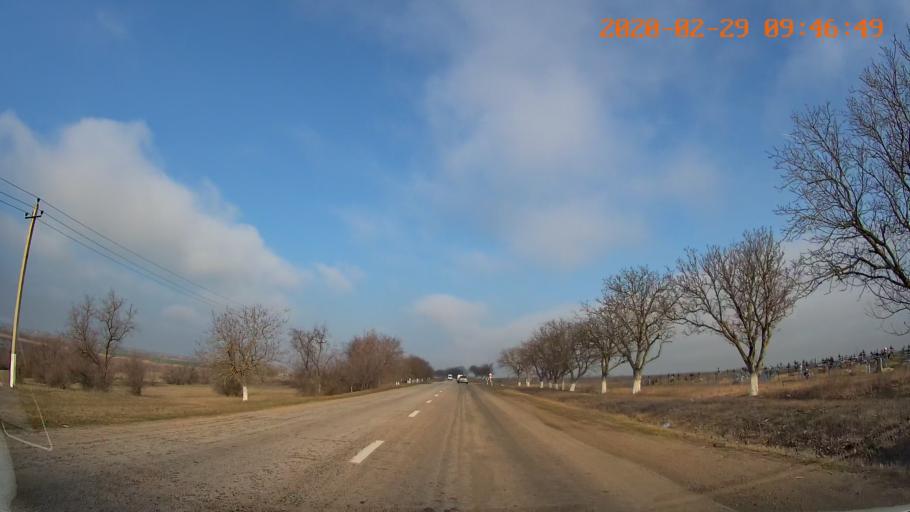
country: MD
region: Telenesti
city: Crasnoe
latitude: 46.6710
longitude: 29.7956
